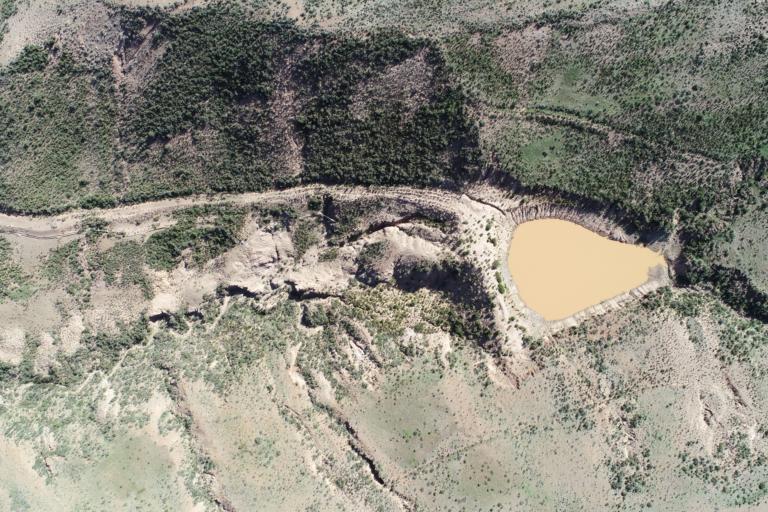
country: BO
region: La Paz
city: Curahuara de Carangas
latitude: -17.3022
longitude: -68.4871
